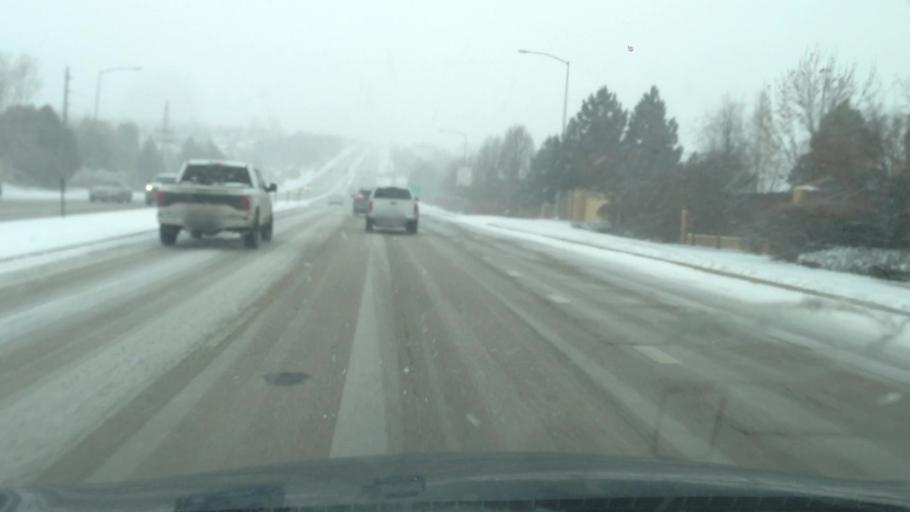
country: US
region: Colorado
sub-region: Arapahoe County
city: Dove Valley
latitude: 39.6341
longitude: -104.8282
